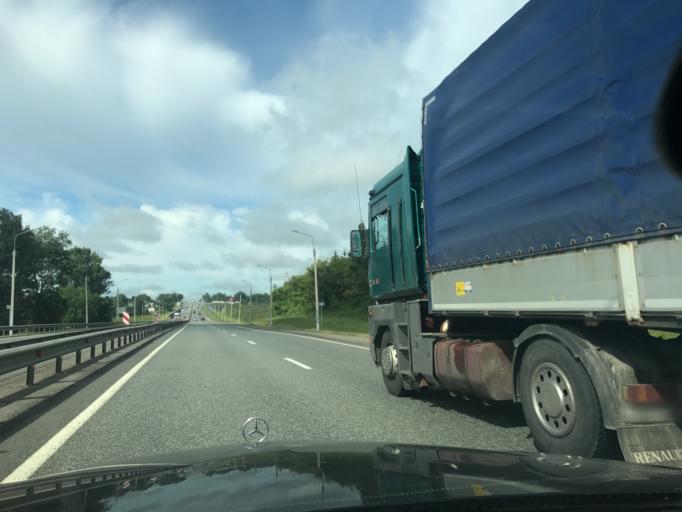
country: RU
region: Smolensk
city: Yartsevo
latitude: 55.0735
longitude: 32.6493
